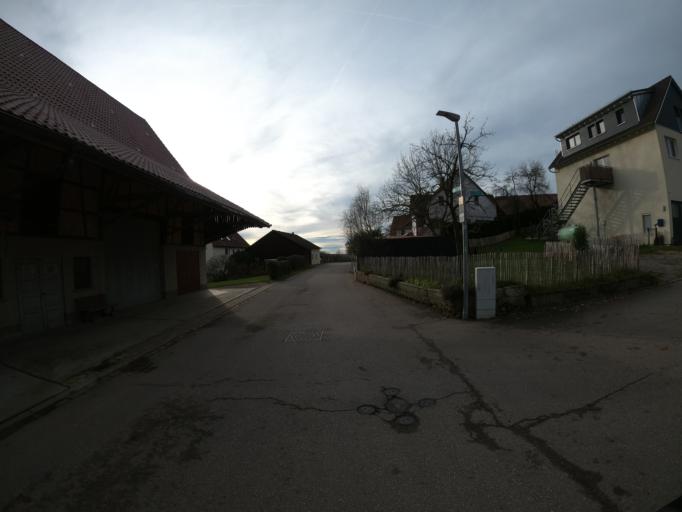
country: DE
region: Baden-Wuerttemberg
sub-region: Regierungsbezirk Stuttgart
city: Waschenbeuren
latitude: 48.7359
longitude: 9.7007
